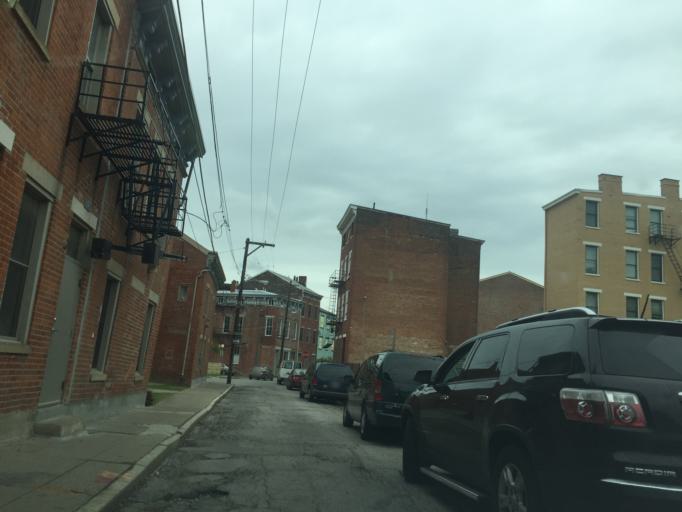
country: US
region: Kentucky
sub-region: Campbell County
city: Newport
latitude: 39.1148
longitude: -84.5154
